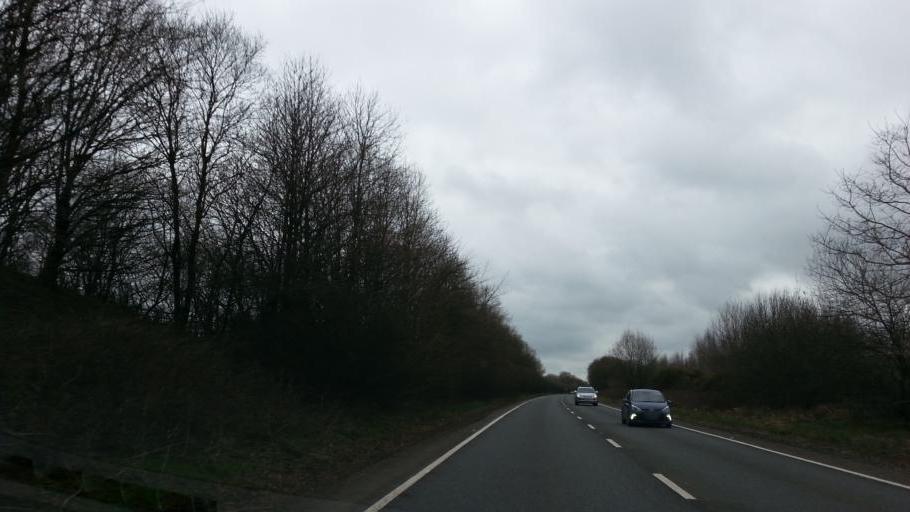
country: GB
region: England
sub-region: Devon
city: South Molton
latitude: 51.0297
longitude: -3.8324
